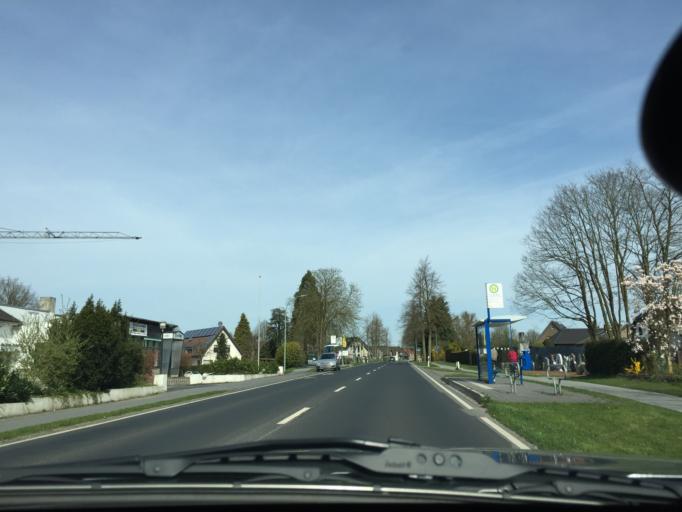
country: DE
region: North Rhine-Westphalia
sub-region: Regierungsbezirk Dusseldorf
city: Goch
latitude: 51.6989
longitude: 6.1562
